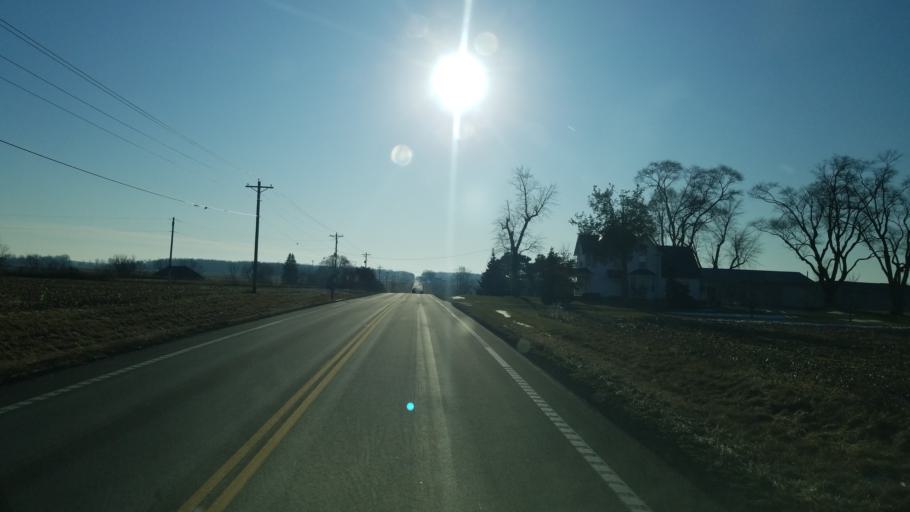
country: US
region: Ohio
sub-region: Sandusky County
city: Green Springs
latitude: 41.1476
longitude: -82.9965
